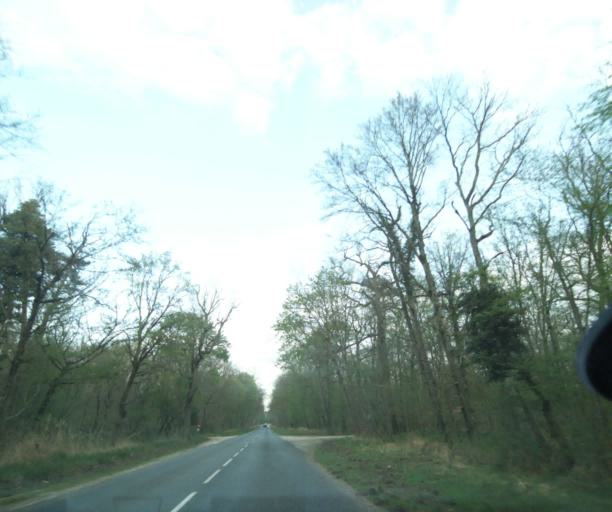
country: FR
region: Ile-de-France
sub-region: Departement de Seine-et-Marne
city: Fontainebleau
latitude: 48.3946
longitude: 2.6984
